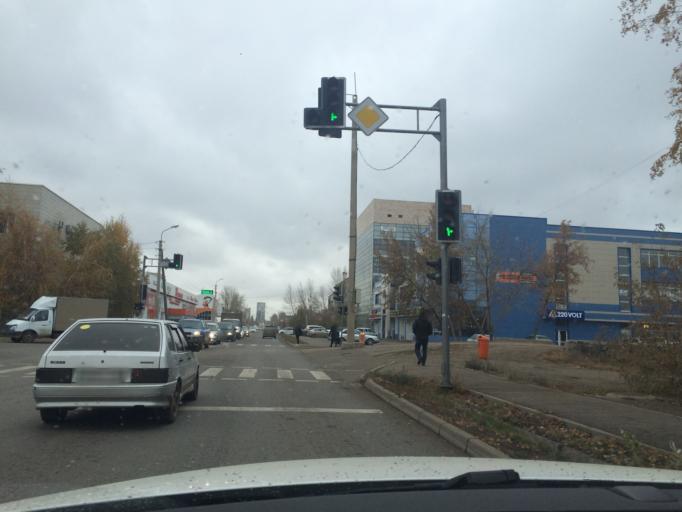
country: KZ
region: Astana Qalasy
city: Astana
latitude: 51.1721
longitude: 71.4523
